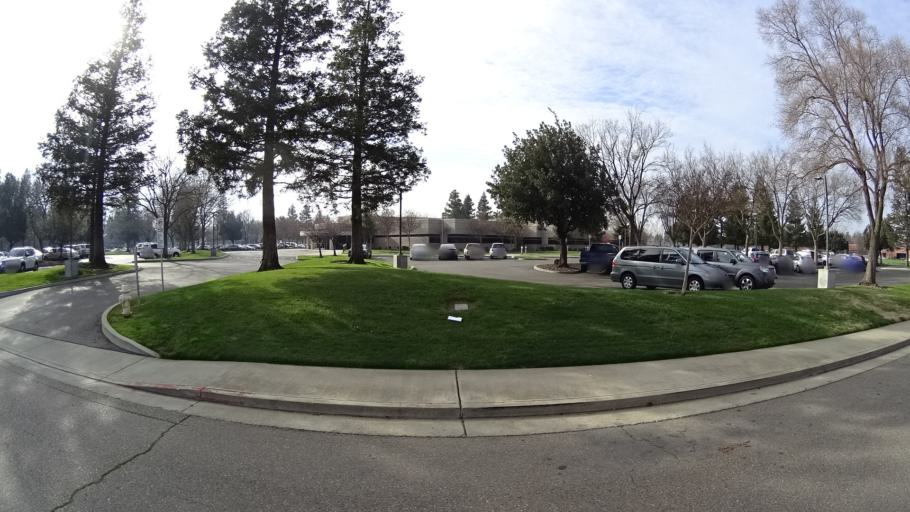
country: US
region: California
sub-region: Yolo County
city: Davis
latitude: 38.5409
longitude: -121.7272
